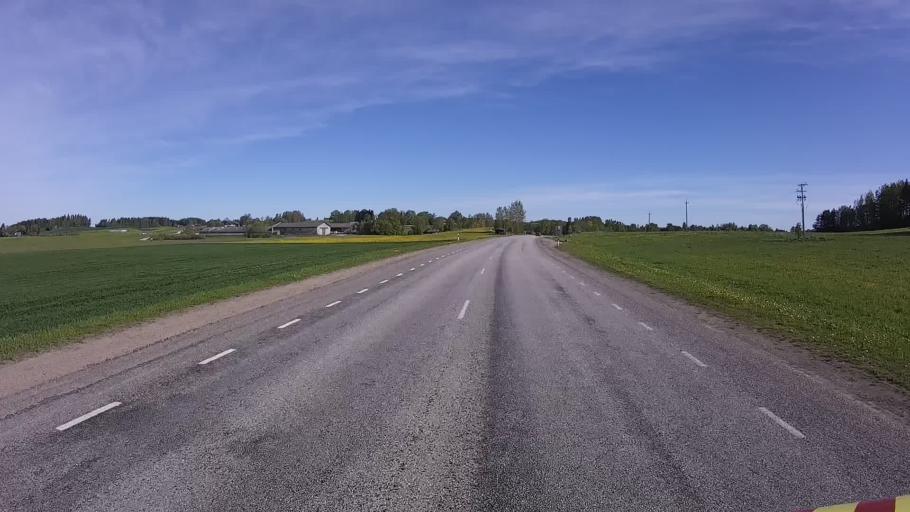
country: EE
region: Tartu
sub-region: Elva linn
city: Elva
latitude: 58.1343
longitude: 26.5219
